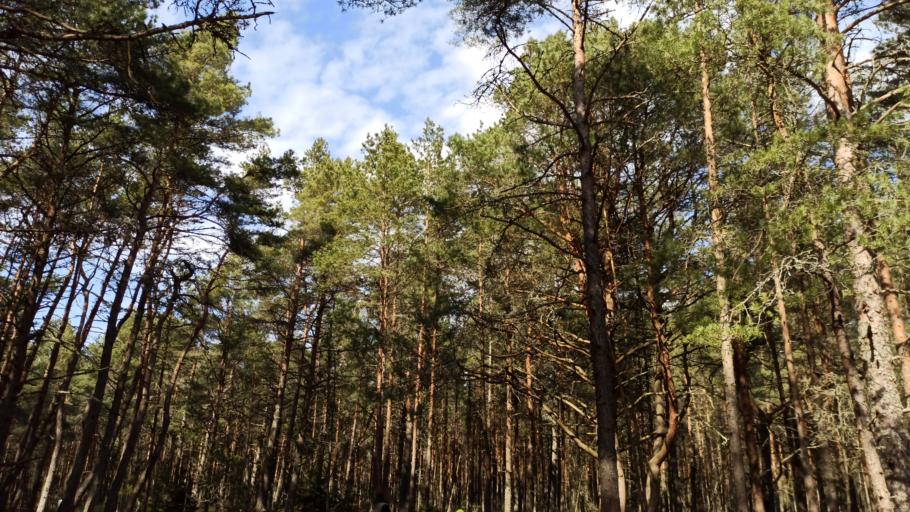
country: LT
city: Nida
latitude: 55.1808
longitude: 20.8637
